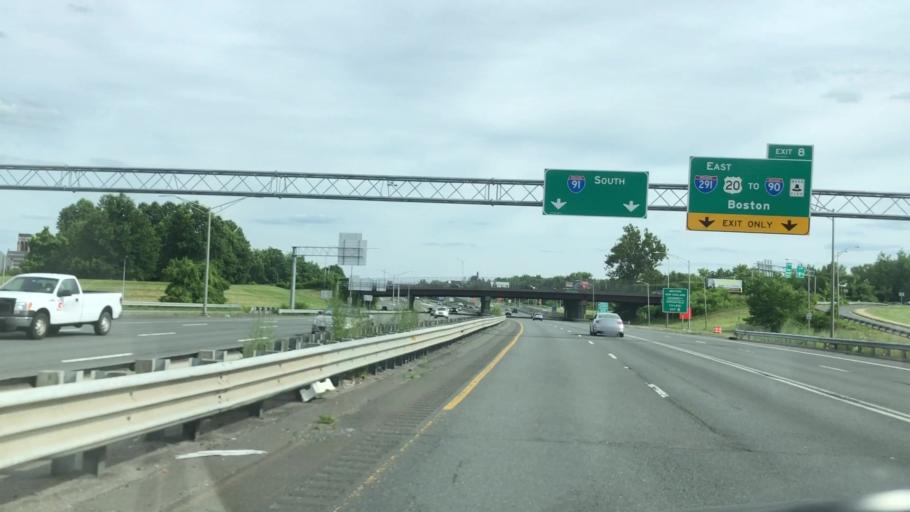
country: US
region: Massachusetts
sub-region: Hampden County
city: West Springfield
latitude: 42.1134
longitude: -72.6077
